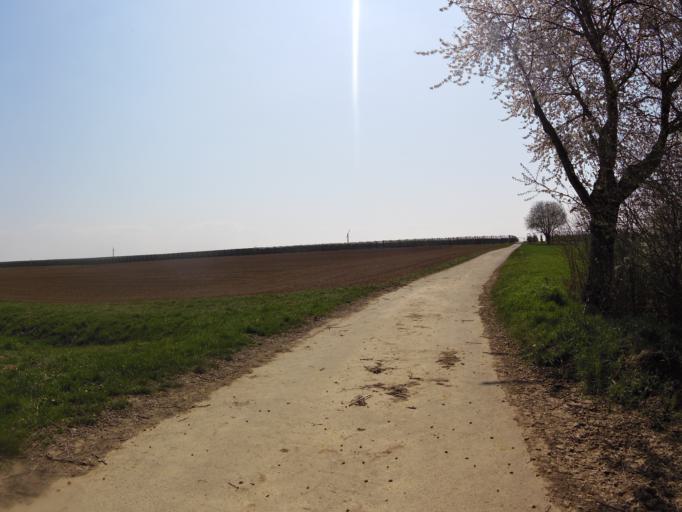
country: DE
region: Bavaria
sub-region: Regierungsbezirk Unterfranken
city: Mainstockheim
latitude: 49.8115
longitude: 10.1126
